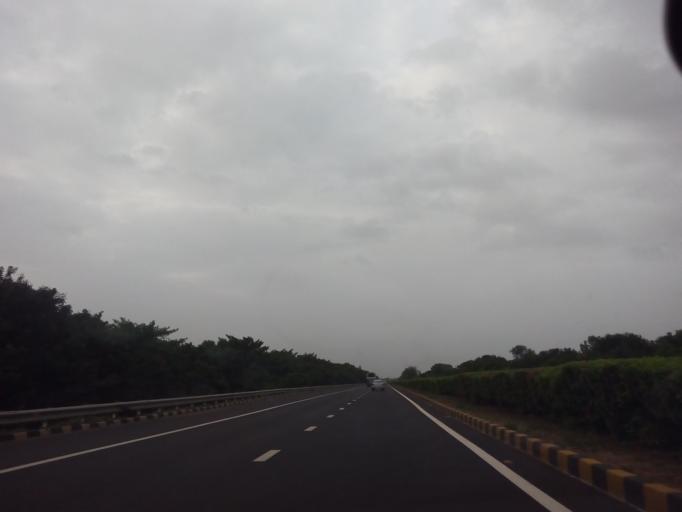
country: IN
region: Gujarat
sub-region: Kheda
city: Nadiad
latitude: 22.6861
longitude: 72.9052
